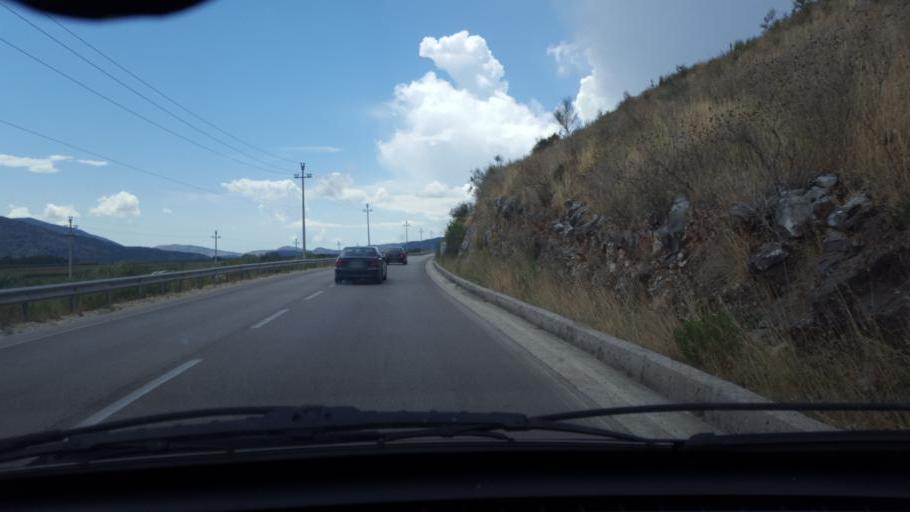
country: AL
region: Vlore
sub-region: Rrethi i Sarandes
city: Sarande
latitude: 39.8310
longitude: 20.0226
